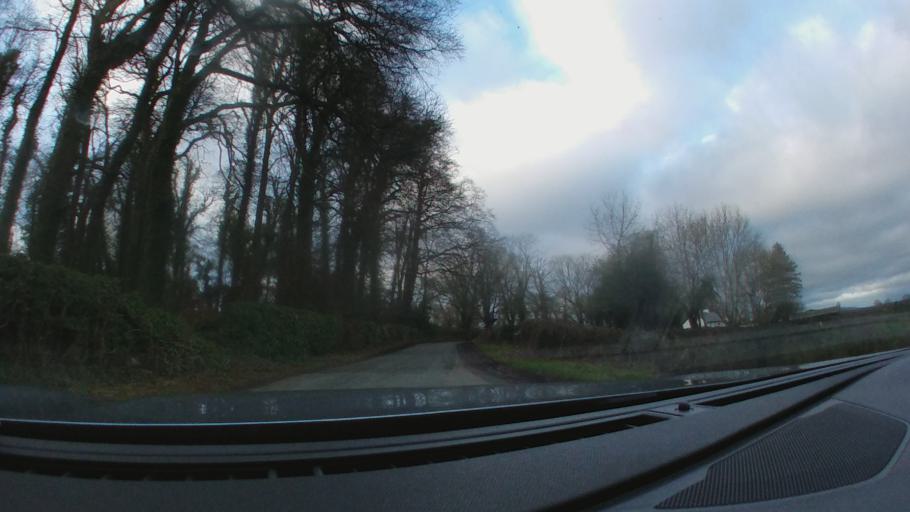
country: IE
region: Leinster
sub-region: Kilkenny
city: Thomastown
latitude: 52.5599
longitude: -7.1362
